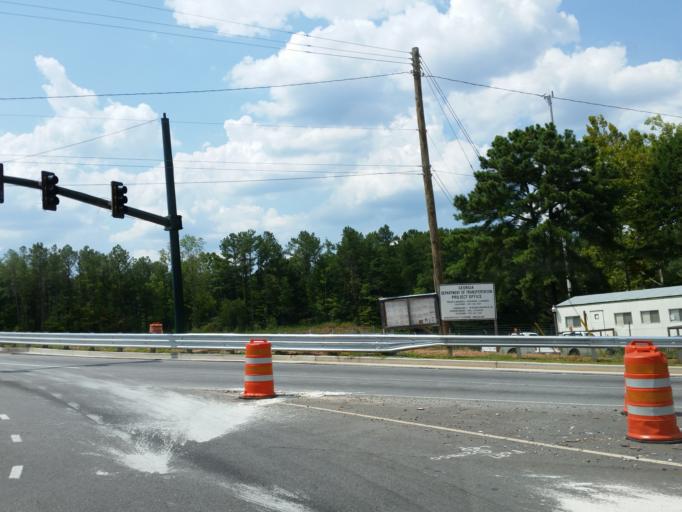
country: US
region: Georgia
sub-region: DeKalb County
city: Dunwoody
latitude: 33.9823
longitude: -84.3405
